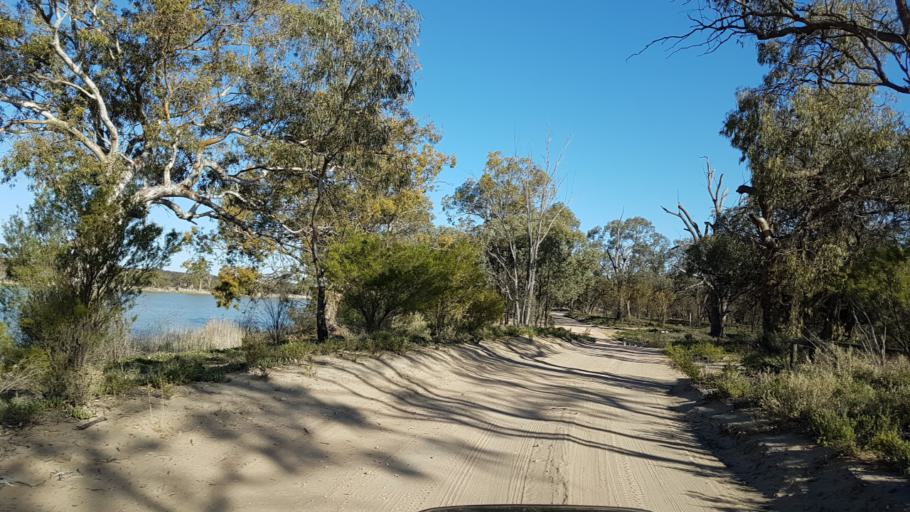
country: AU
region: South Australia
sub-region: Loxton Waikerie
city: Waikerie
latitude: -34.1605
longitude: 140.0309
